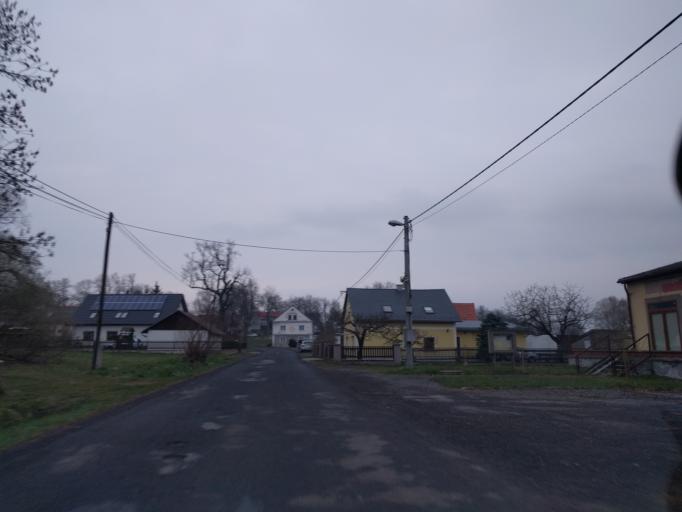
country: CZ
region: Karlovarsky
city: Bochov
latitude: 50.1340
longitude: 13.0871
